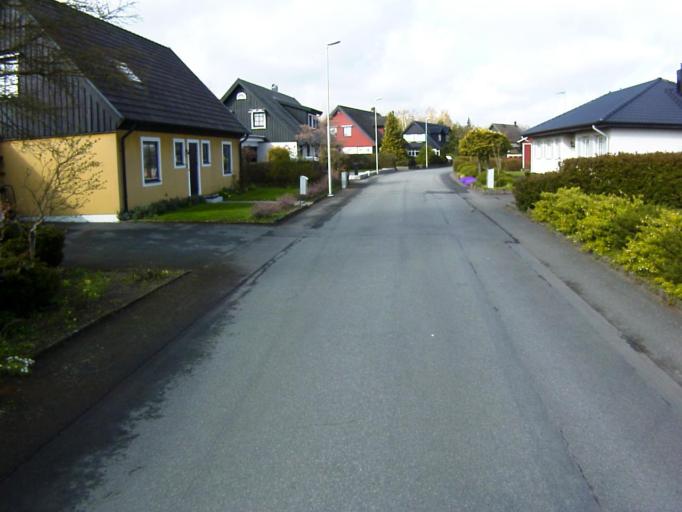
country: SE
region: Skane
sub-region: Kristianstads Kommun
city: Kristianstad
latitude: 56.0107
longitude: 14.1050
